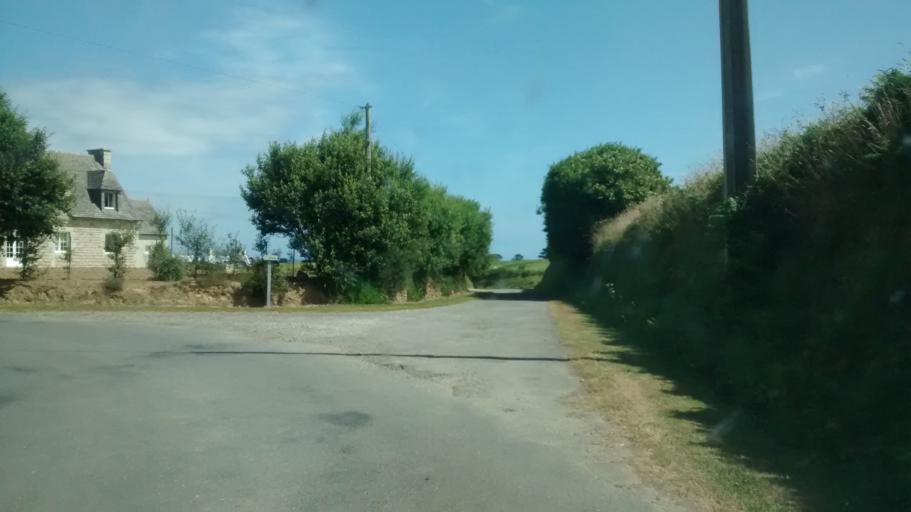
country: FR
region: Brittany
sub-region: Departement du Finistere
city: Plouguerneau
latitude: 48.6178
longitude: -4.4789
